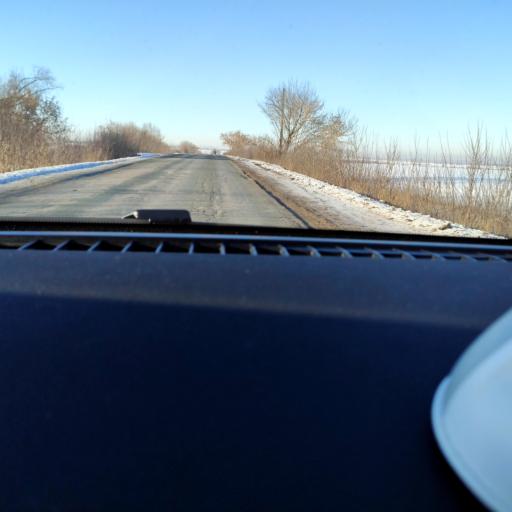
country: RU
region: Samara
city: Spiridonovka
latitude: 53.1446
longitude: 50.5786
